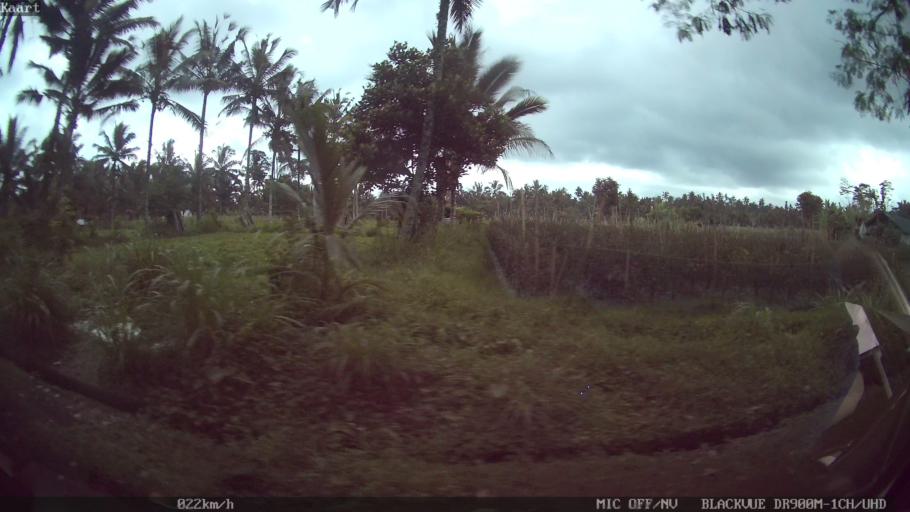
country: ID
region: Bali
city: Banjar Wangsian
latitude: -8.4426
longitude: 115.4254
